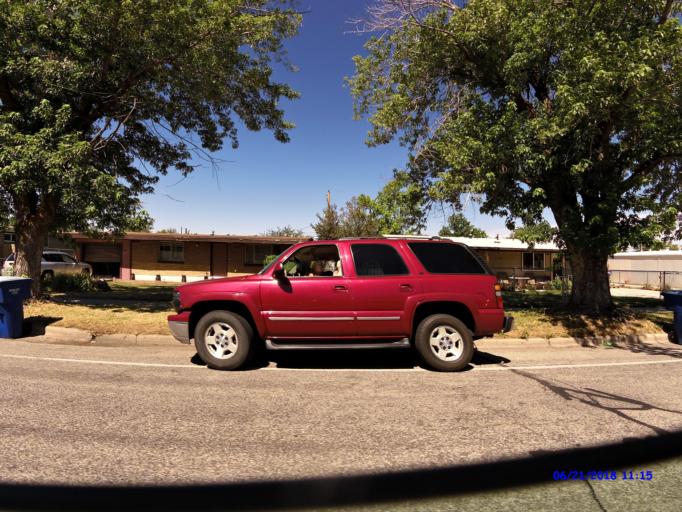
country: US
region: Utah
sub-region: Weber County
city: Harrisville
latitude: 41.2713
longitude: -111.9592
